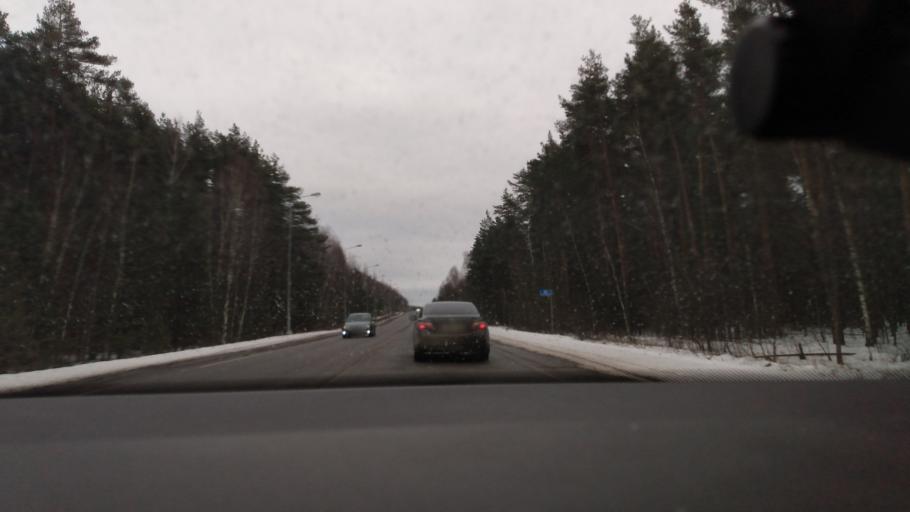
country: RU
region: Moskovskaya
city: Il'inskiy Pogost
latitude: 55.4879
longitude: 38.8973
